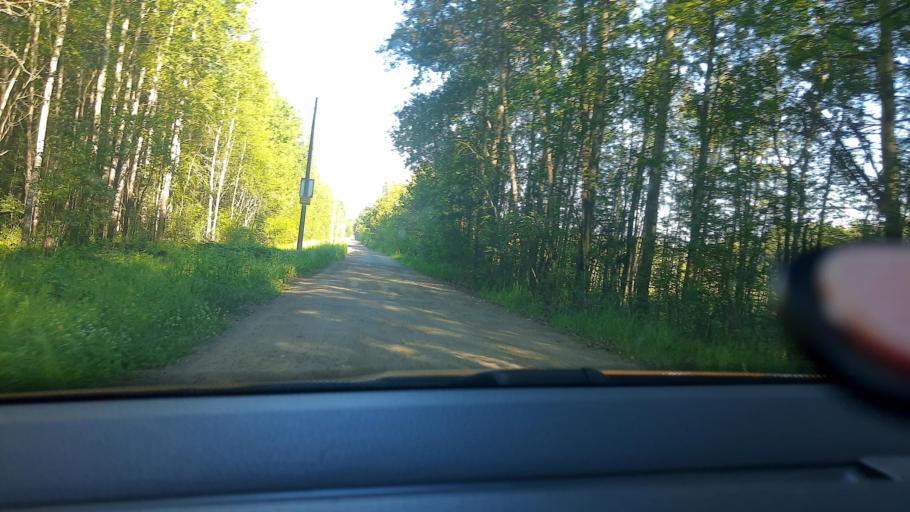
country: RU
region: Moskovskaya
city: Elektrogorsk
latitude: 55.8976
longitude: 38.7121
